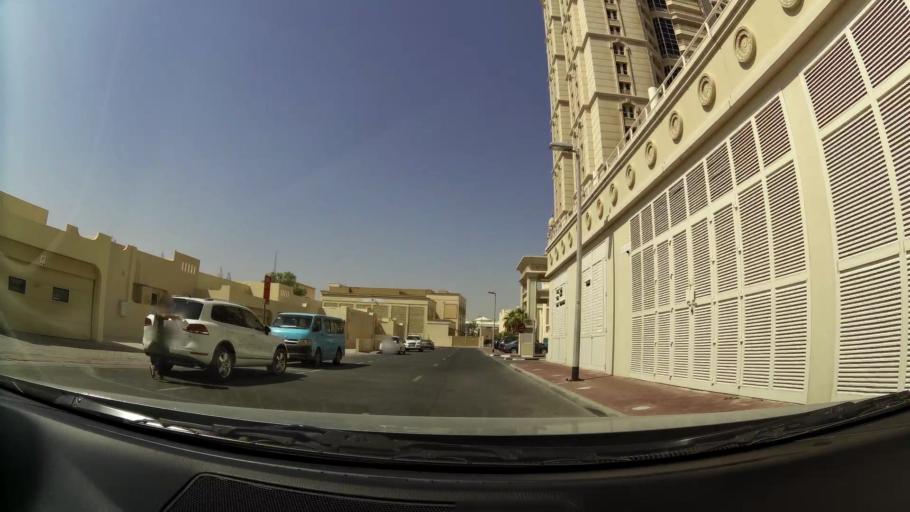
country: AE
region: Ash Shariqah
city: Sharjah
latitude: 25.2372
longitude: 55.2729
